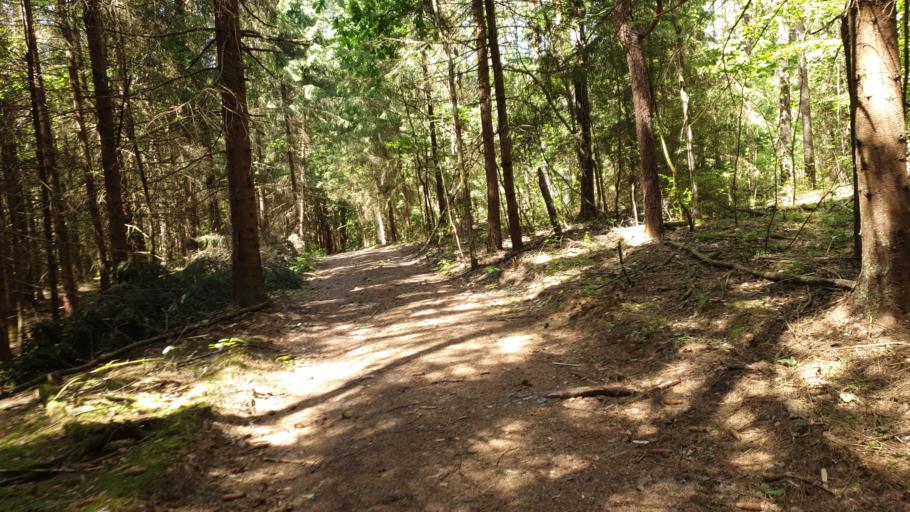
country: LT
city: Grigiskes
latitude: 54.7794
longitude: 24.9926
